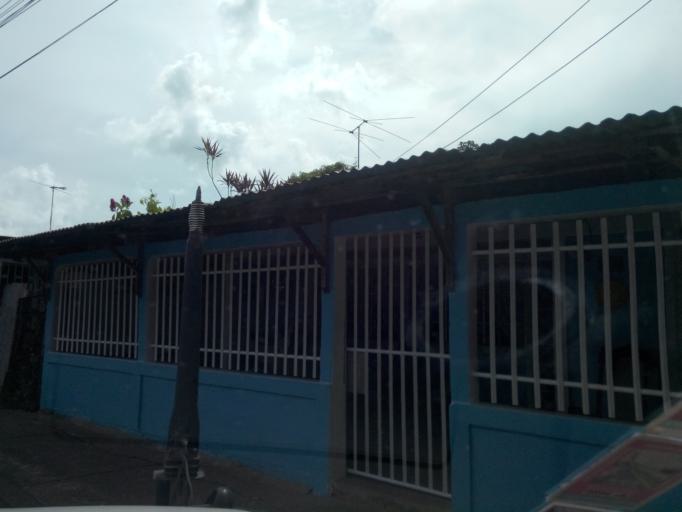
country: NI
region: Atlantico Sur
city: Bluefields
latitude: 11.9990
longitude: -83.7687
